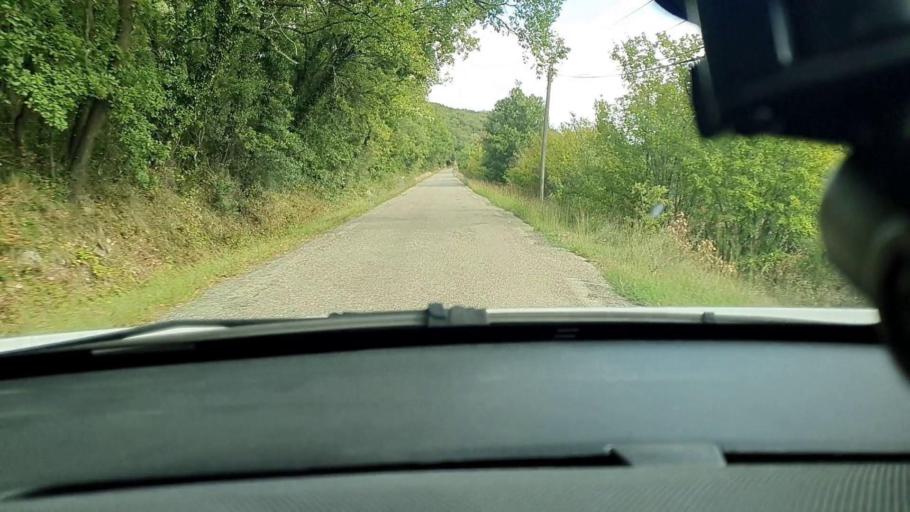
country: FR
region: Languedoc-Roussillon
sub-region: Departement du Gard
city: Mons
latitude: 44.1677
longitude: 4.2839
